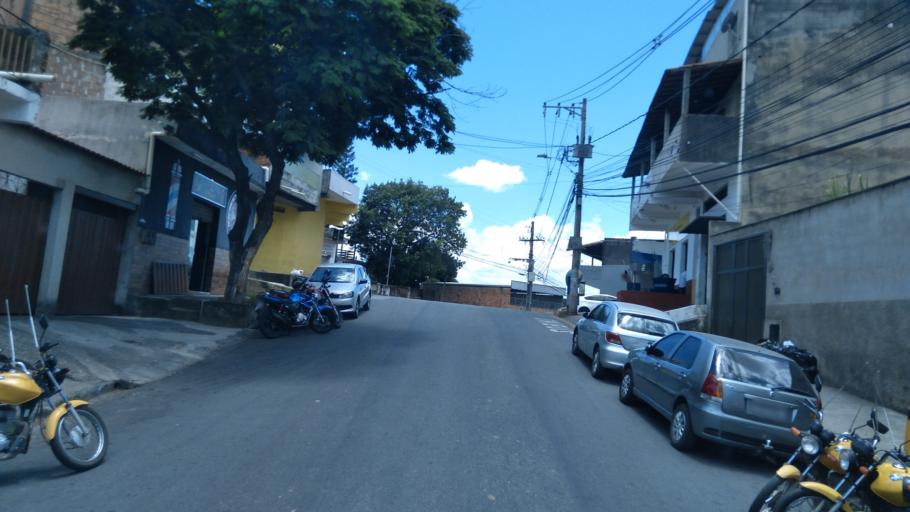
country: BR
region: Minas Gerais
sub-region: Belo Horizonte
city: Belo Horizonte
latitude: -19.8459
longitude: -43.8967
